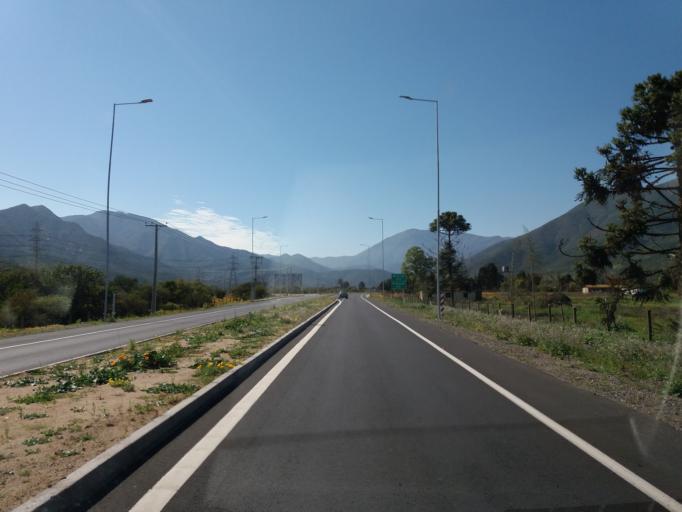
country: CL
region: Valparaiso
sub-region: Provincia de Marga Marga
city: Limache
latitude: -33.0193
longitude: -71.1739
